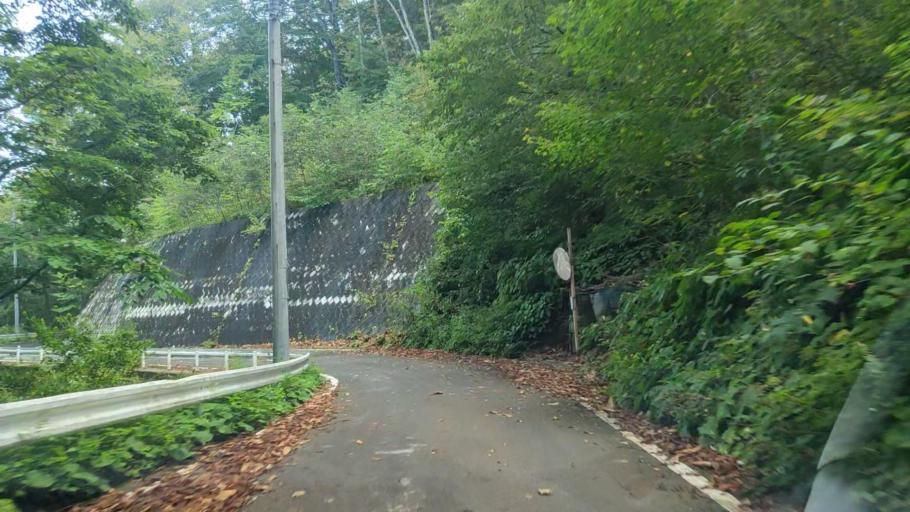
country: JP
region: Gunma
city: Nakanojomachi
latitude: 36.6503
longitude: 138.6226
